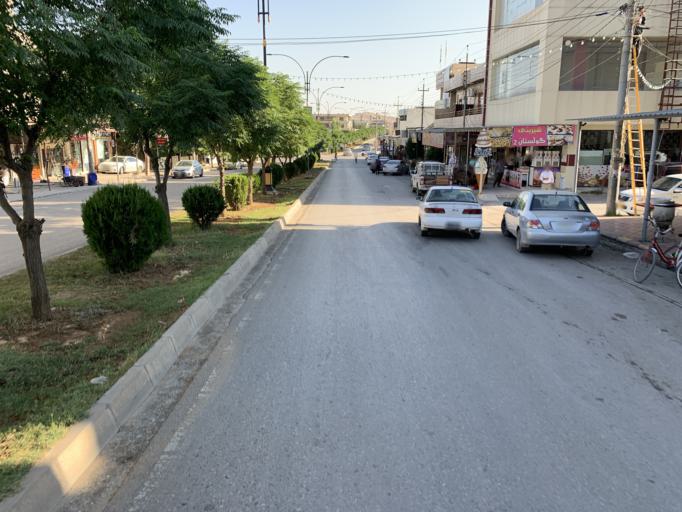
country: IQ
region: As Sulaymaniyah
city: Raniye
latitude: 36.2481
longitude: 44.8755
